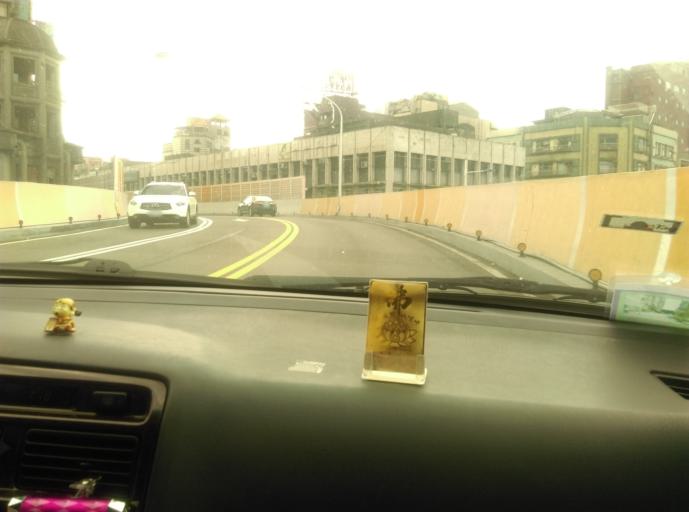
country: TW
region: Taiwan
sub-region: Keelung
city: Keelung
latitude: 25.1303
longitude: 121.7423
